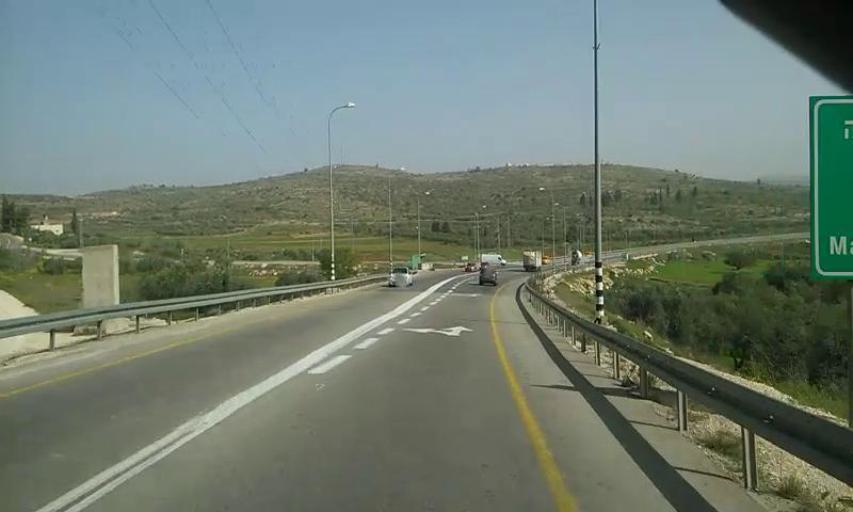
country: PS
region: West Bank
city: Turmus`ayya
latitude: 32.0387
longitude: 35.2752
